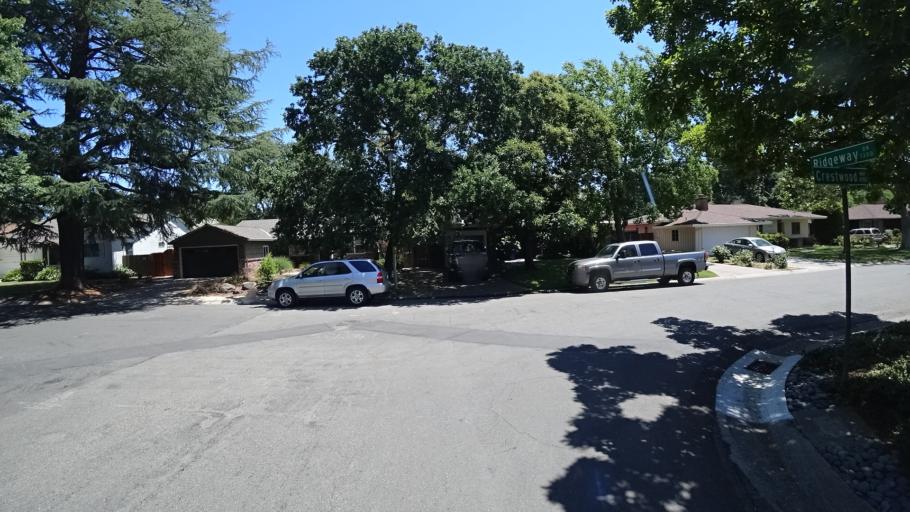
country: US
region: California
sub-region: Sacramento County
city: Sacramento
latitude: 38.5323
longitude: -121.5063
